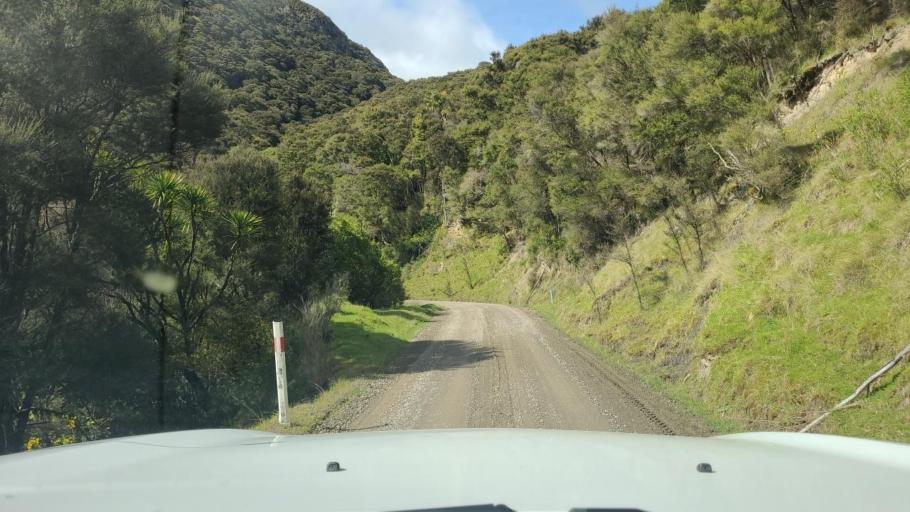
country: NZ
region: Wellington
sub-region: South Wairarapa District
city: Waipawa
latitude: -41.3488
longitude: 175.6777
